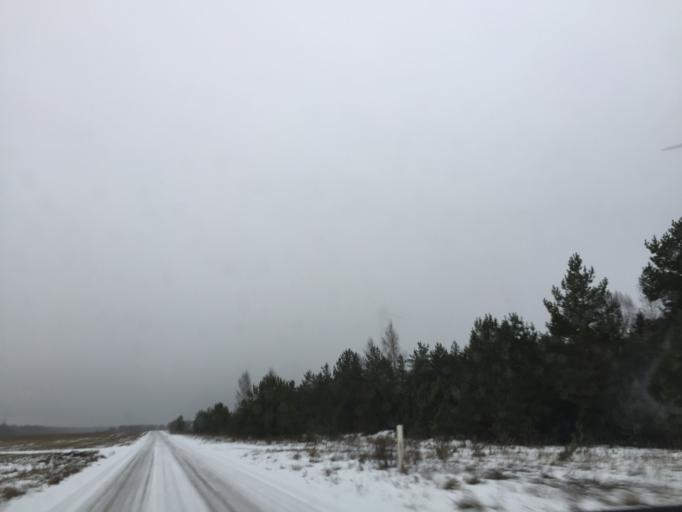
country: EE
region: Laeaene
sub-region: Lihula vald
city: Lihula
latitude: 58.6260
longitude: 23.5375
